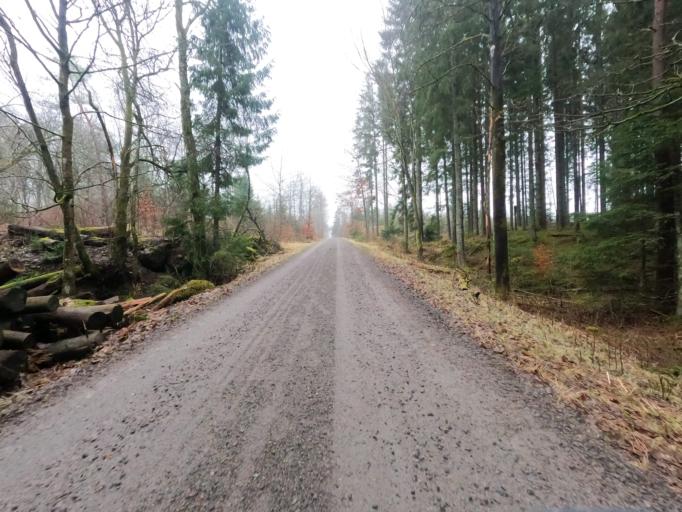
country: SE
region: Halland
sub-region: Hylte Kommun
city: Hyltebruk
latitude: 56.8056
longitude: 13.3240
